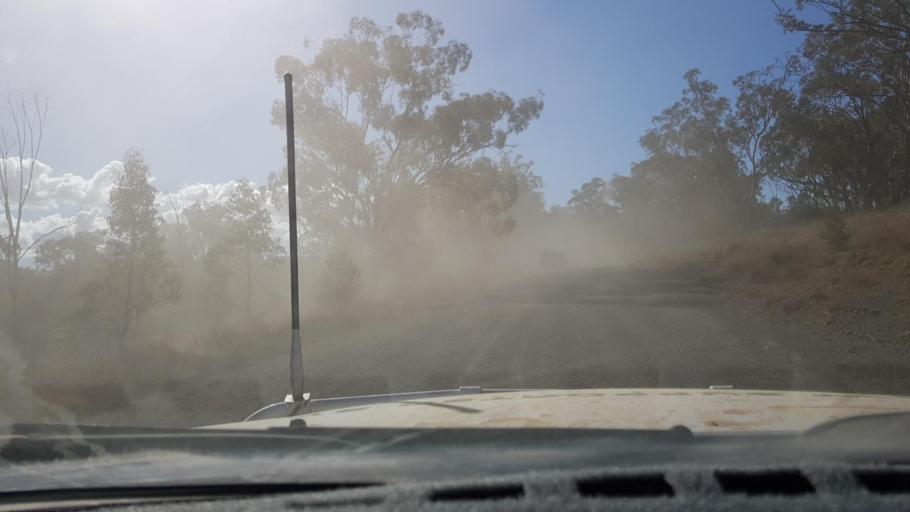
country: AU
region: New South Wales
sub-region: Tamworth Municipality
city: Manilla
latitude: -30.6627
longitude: 150.4667
